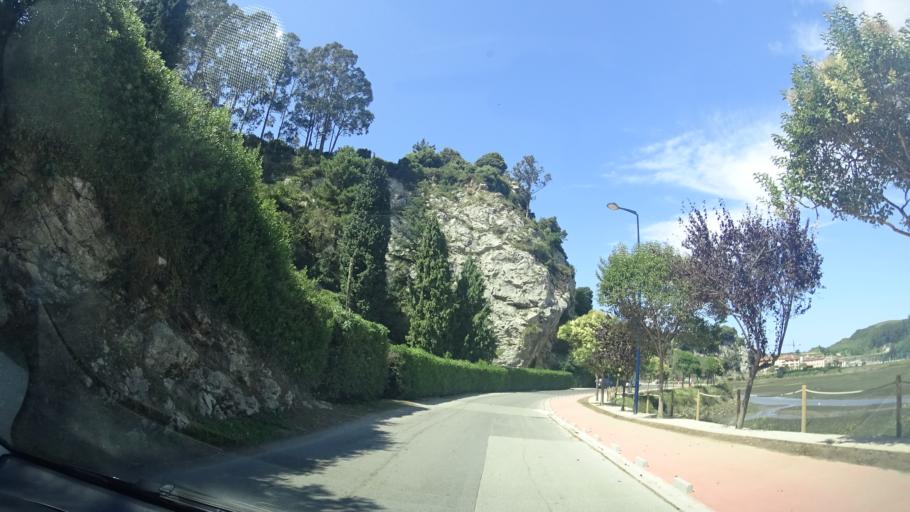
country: ES
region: Asturias
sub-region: Province of Asturias
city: Ribadesella
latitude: 43.4591
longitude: -5.0673
